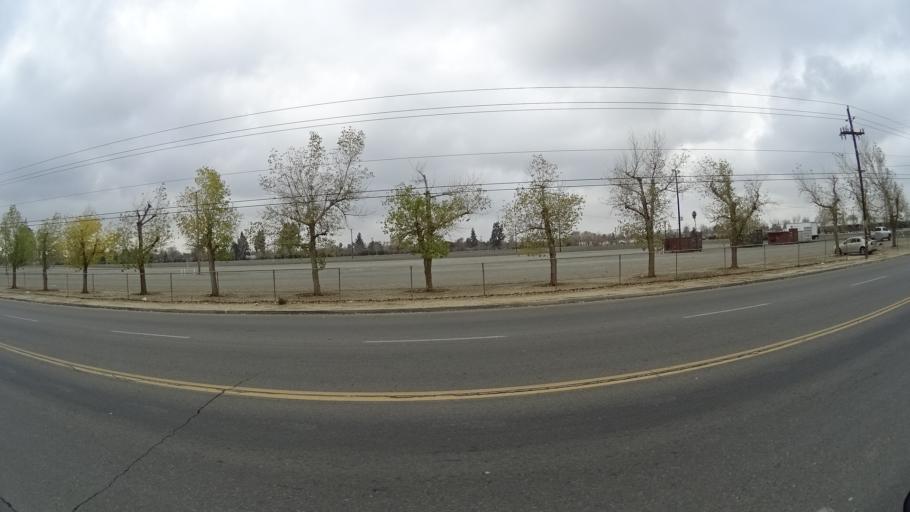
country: US
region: California
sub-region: Kern County
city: Bakersfield
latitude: 35.3450
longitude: -119.0118
